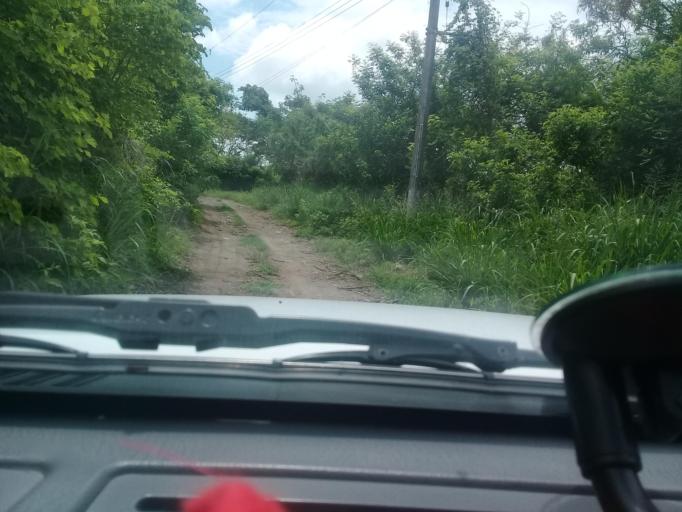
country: MX
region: Veracruz
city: Paso de Ovejas
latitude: 19.2819
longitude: -96.4283
